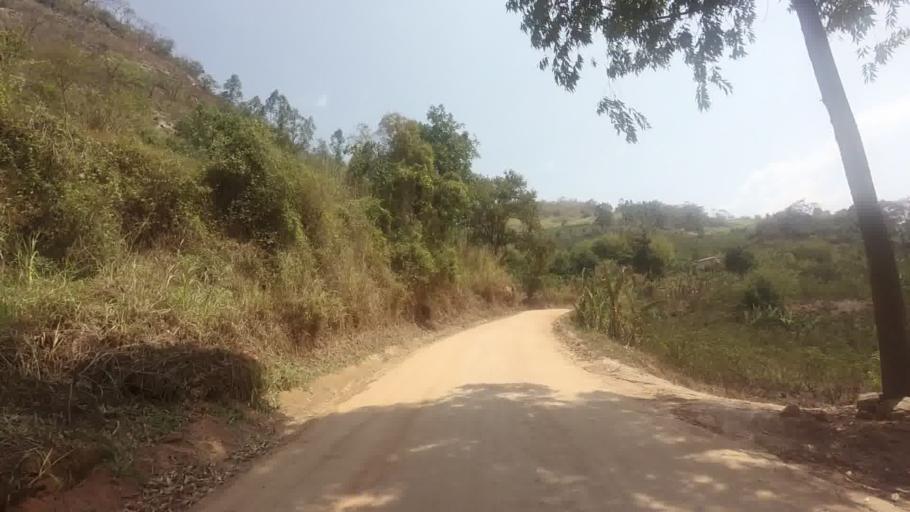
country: BR
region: Espirito Santo
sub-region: Mimoso Do Sul
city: Mimoso do Sul
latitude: -20.9470
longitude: -41.3939
